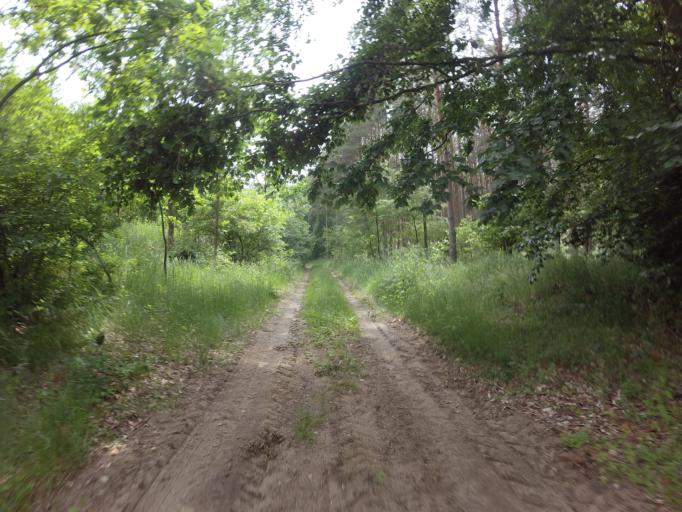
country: PL
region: West Pomeranian Voivodeship
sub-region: Powiat stargardzki
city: Dobrzany
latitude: 53.3292
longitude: 15.4680
